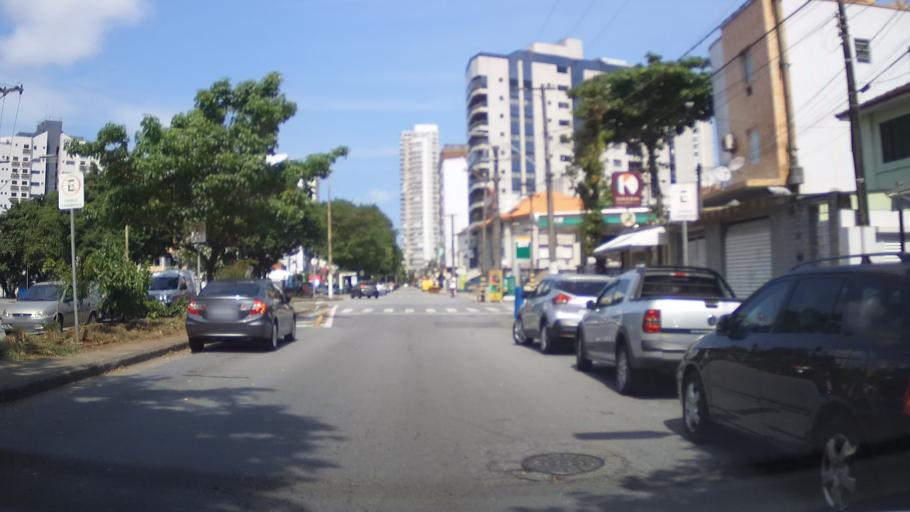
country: BR
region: Sao Paulo
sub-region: Santos
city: Santos
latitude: -23.9866
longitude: -46.3037
